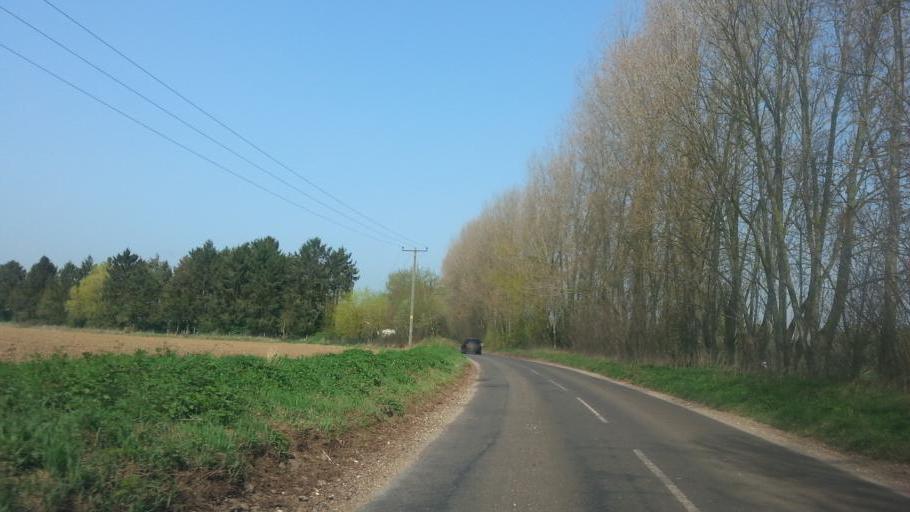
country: GB
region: England
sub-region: Suffolk
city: Thurston
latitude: 52.2393
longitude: 0.8267
